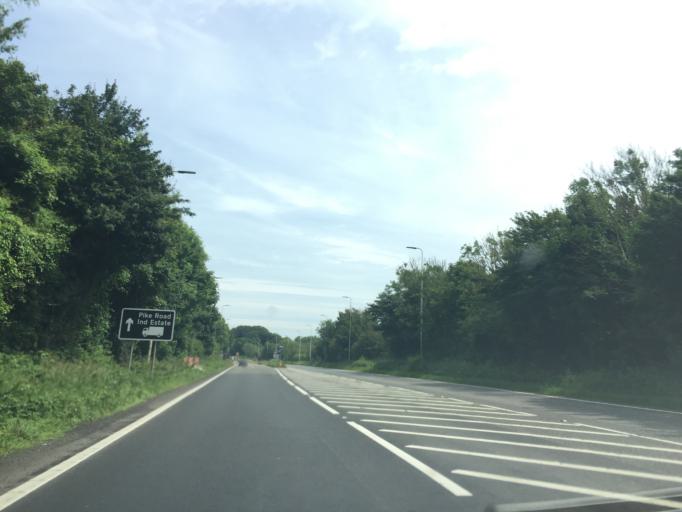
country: GB
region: England
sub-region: Kent
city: Dover
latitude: 51.1563
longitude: 1.2824
